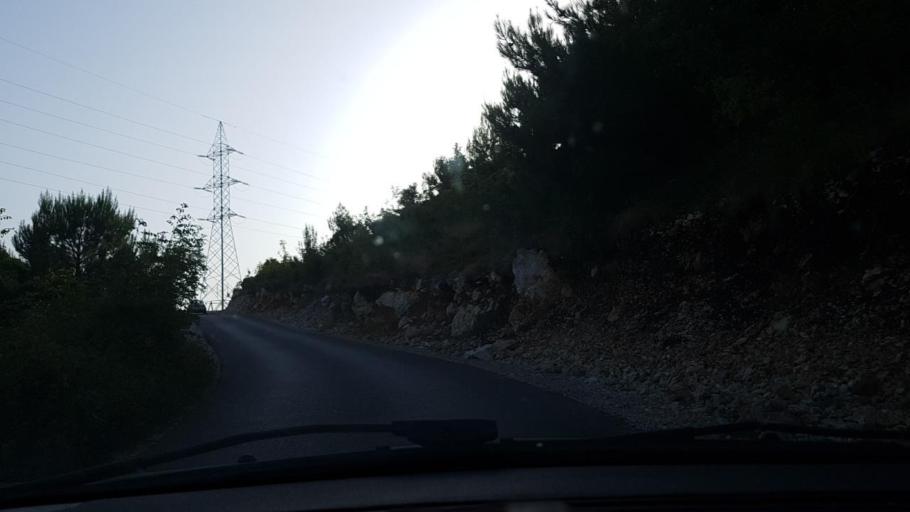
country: BA
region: Federation of Bosnia and Herzegovina
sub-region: Hercegovacko-Bosanski Kanton
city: Mostar
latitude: 43.3501
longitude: 17.8353
